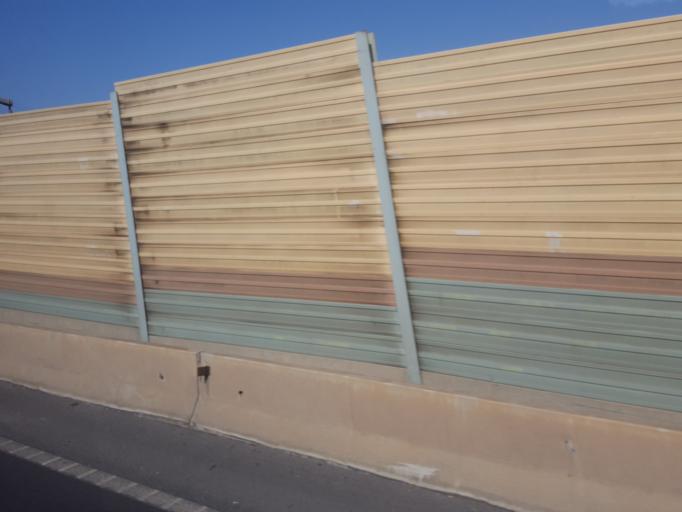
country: ES
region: Murcia
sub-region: Murcia
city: Murcia
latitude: 38.0014
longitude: -1.1590
